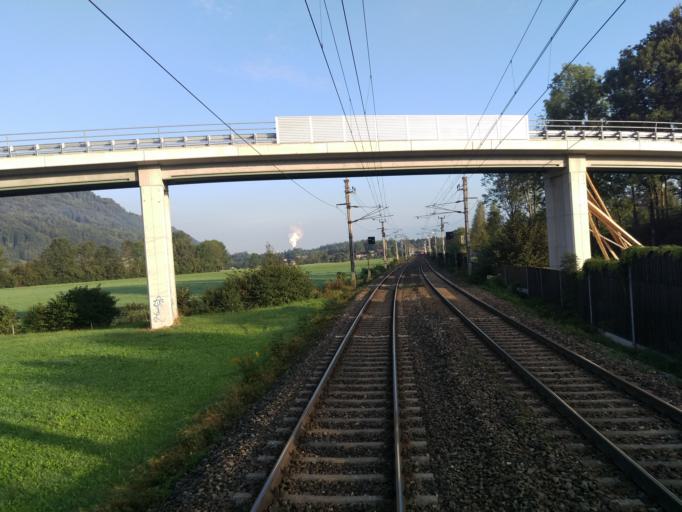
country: AT
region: Salzburg
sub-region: Politischer Bezirk Hallein
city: Kuchl
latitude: 47.6451
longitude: 13.1310
